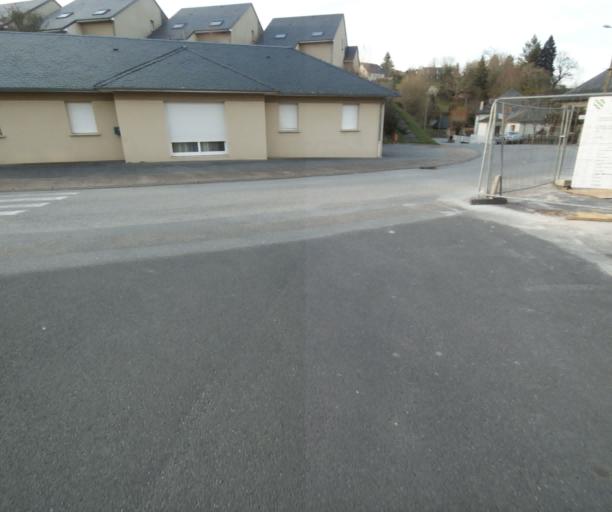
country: FR
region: Limousin
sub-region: Departement de la Correze
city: Correze
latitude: 45.3681
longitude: 1.8719
